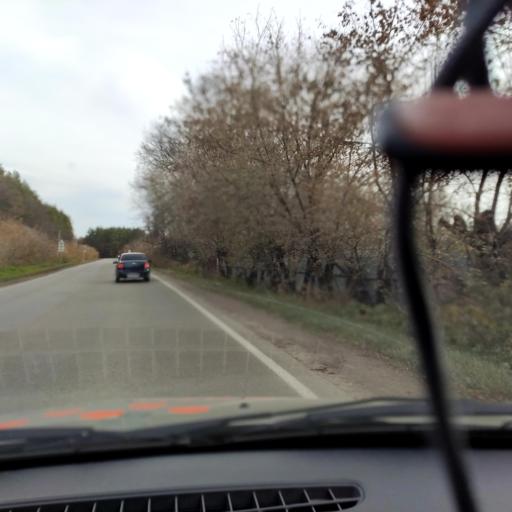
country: RU
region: Bashkortostan
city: Ufa
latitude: 54.5634
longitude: 55.9550
